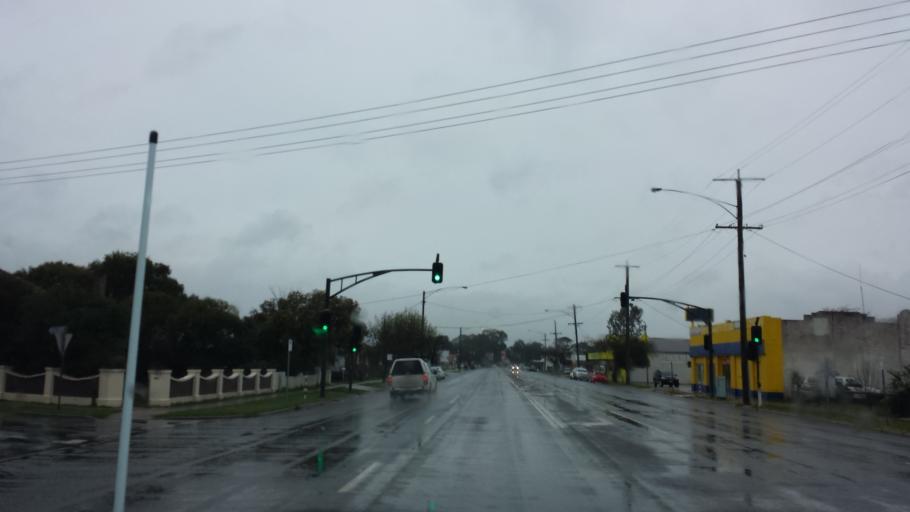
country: AU
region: Victoria
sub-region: Benalla
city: Benalla
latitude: -36.5498
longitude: 145.9919
